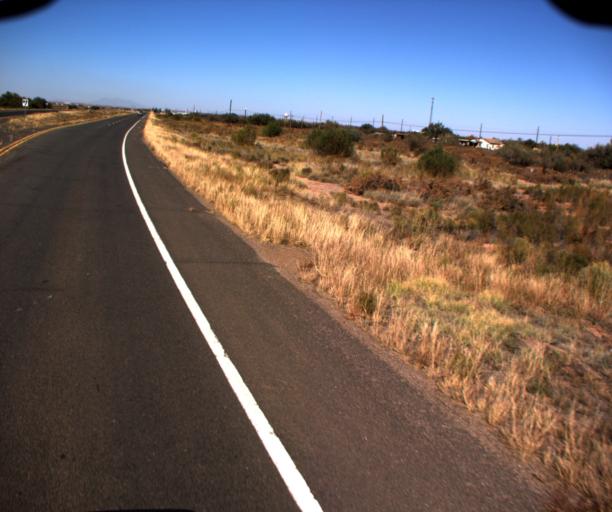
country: US
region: Arizona
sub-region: Navajo County
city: Winslow
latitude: 35.0077
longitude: -110.6598
